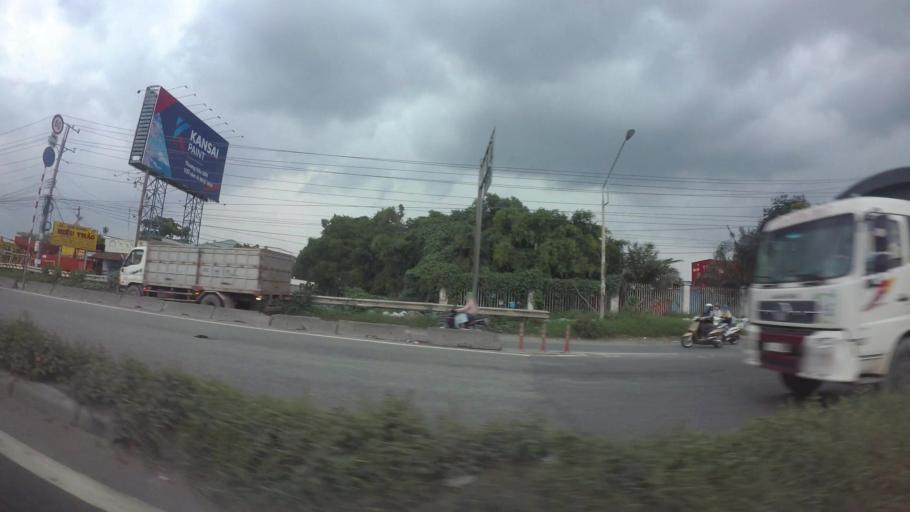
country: VN
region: Dong Nai
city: Bien Hoa
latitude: 10.8972
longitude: 106.8279
